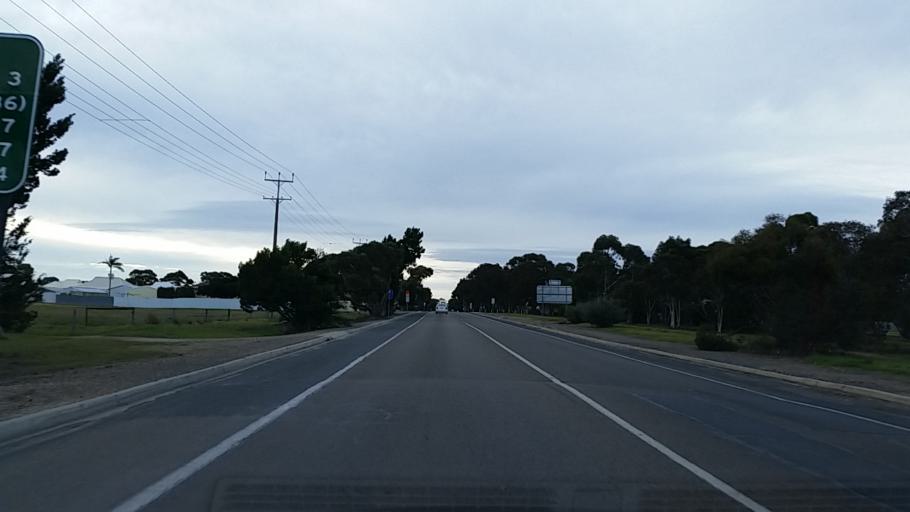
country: AU
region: South Australia
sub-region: Murray Bridge
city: Murray Bridge
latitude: -35.1472
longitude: 139.2861
